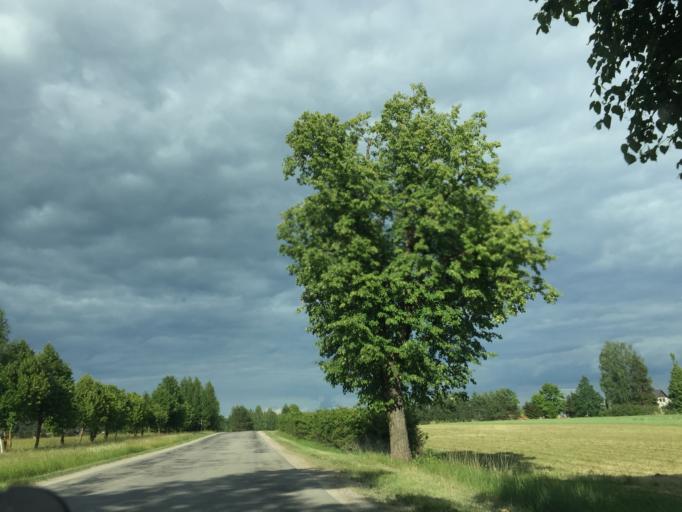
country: LV
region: Skriveri
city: Skriveri
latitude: 56.8378
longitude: 25.1374
